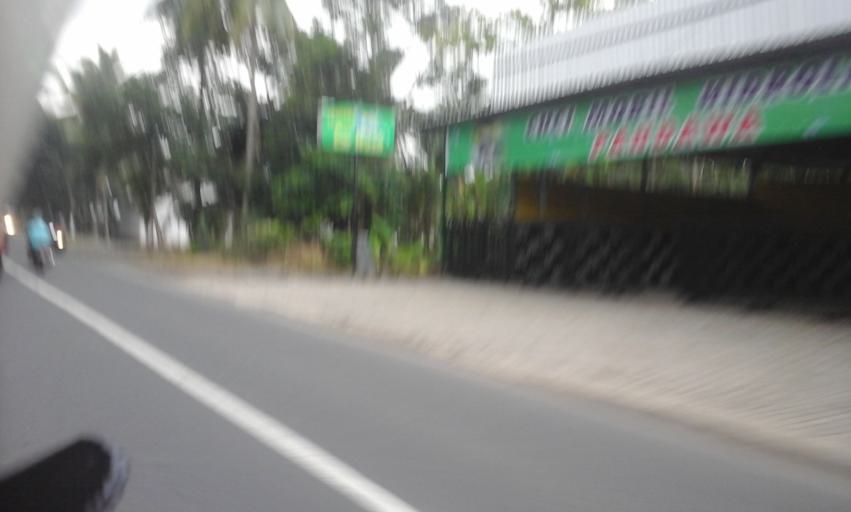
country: ID
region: East Java
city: Klompangan
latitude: -8.2376
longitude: 113.6546
